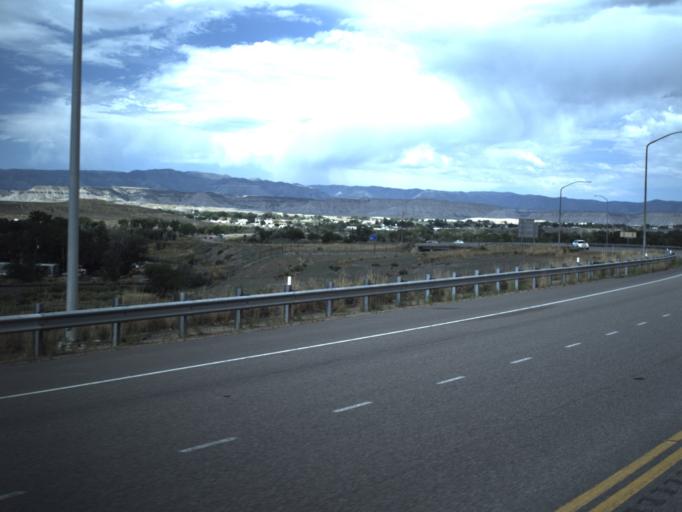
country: US
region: Utah
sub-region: Carbon County
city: Price
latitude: 39.5872
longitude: -110.7894
